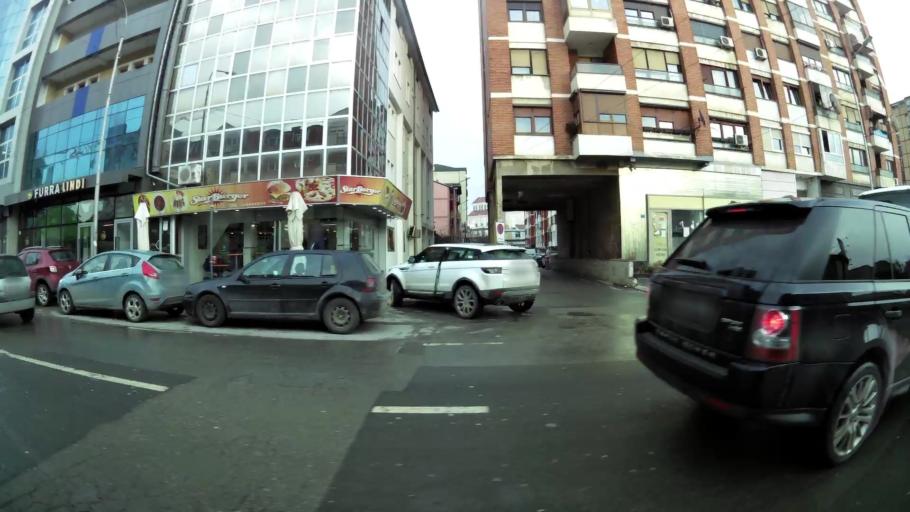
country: XK
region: Pristina
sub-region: Komuna e Prishtines
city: Pristina
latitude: 42.6555
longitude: 21.1555
